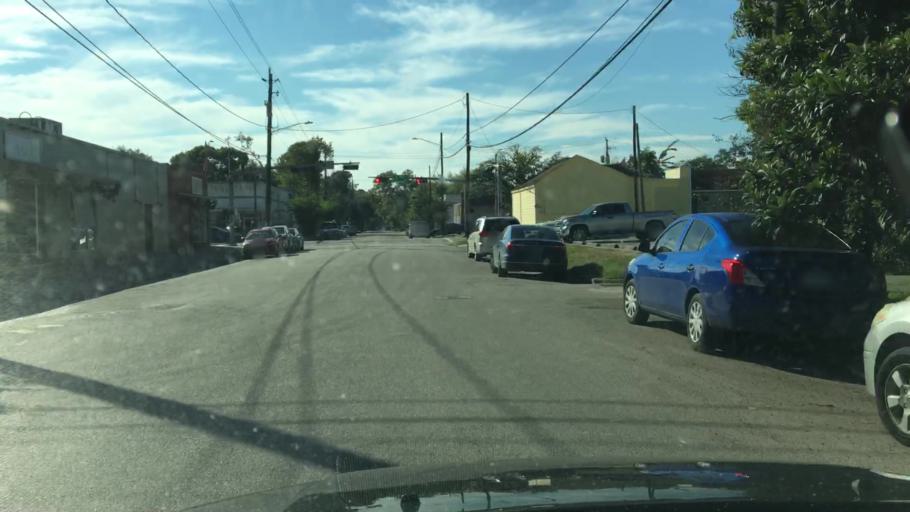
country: US
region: Texas
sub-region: Harris County
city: Houston
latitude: 29.8036
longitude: -95.4014
